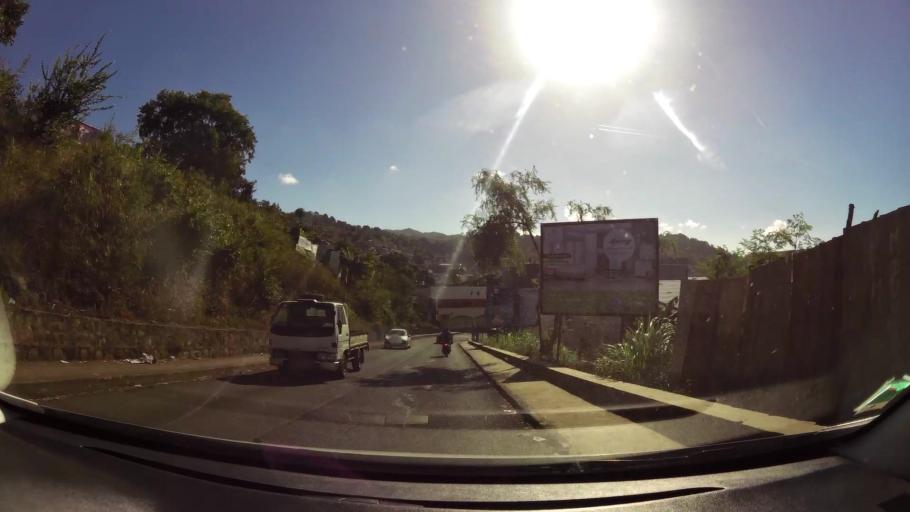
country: YT
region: Mamoudzou
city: Mamoudzou
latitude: -12.7763
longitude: 45.2250
